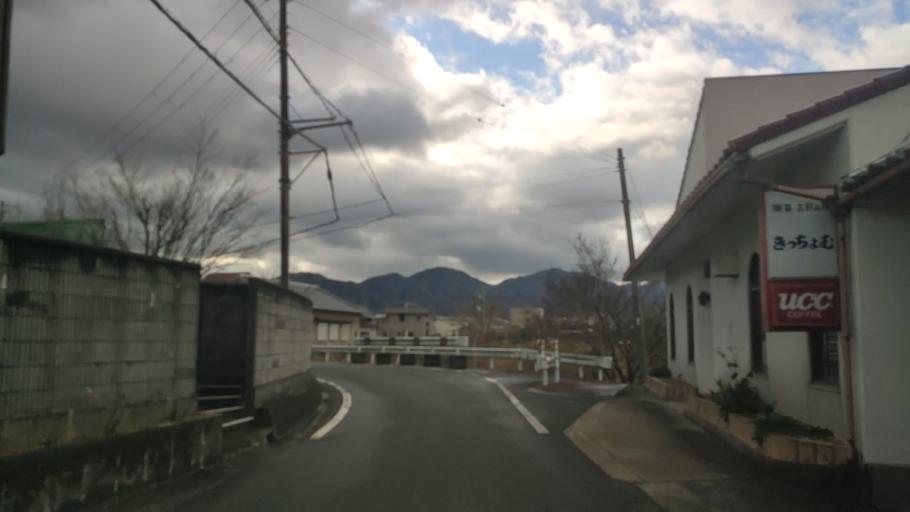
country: JP
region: Hyogo
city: Sumoto
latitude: 34.3273
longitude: 134.8535
